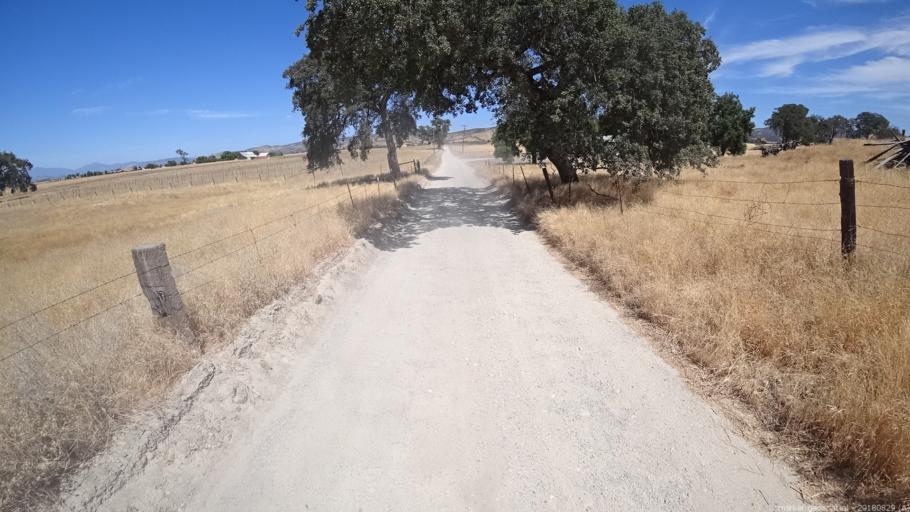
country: US
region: California
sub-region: Monterey County
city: King City
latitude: 35.9400
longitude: -121.0732
